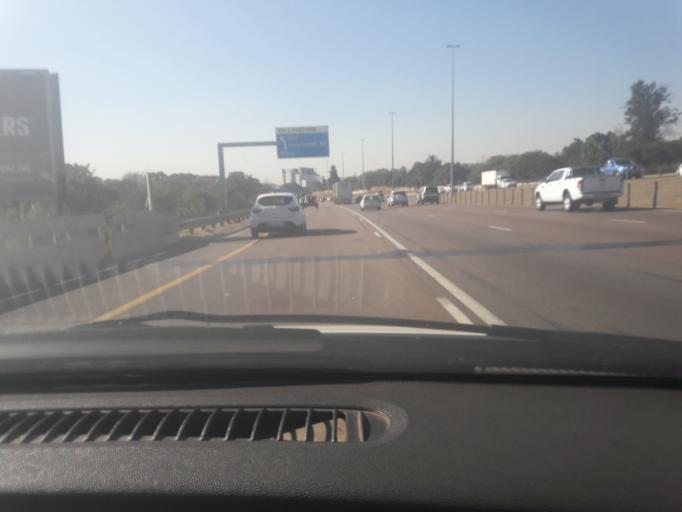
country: ZA
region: Gauteng
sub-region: City of Tshwane Metropolitan Municipality
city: Pretoria
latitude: -25.7935
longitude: 28.2668
